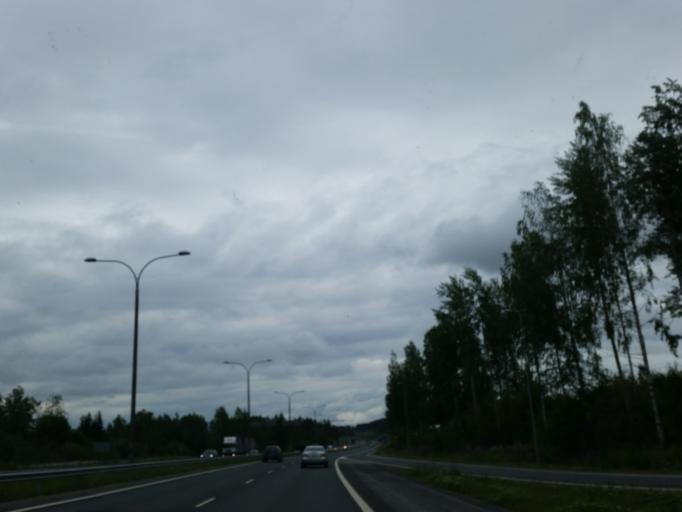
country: FI
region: Northern Savo
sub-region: Kuopio
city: Kuopio
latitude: 62.9599
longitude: 27.6917
